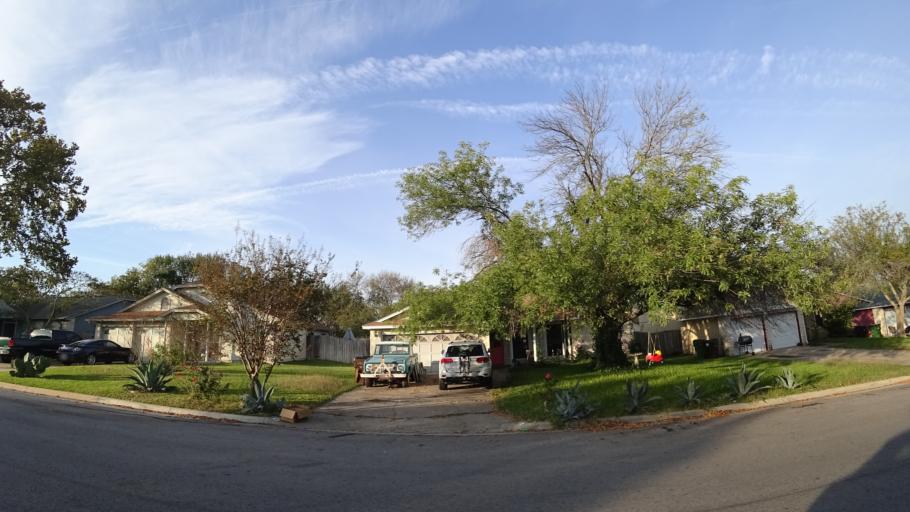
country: US
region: Texas
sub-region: Williamson County
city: Round Rock
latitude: 30.5024
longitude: -97.6675
